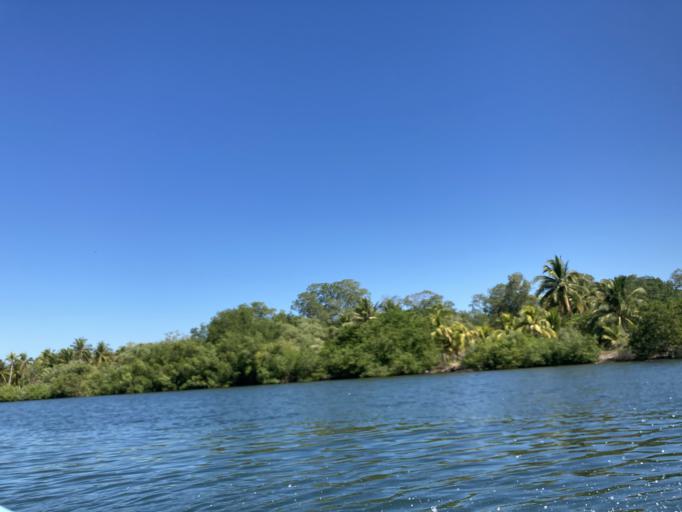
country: GT
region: Jutiapa
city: Pasaco
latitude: 13.8066
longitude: -90.2699
